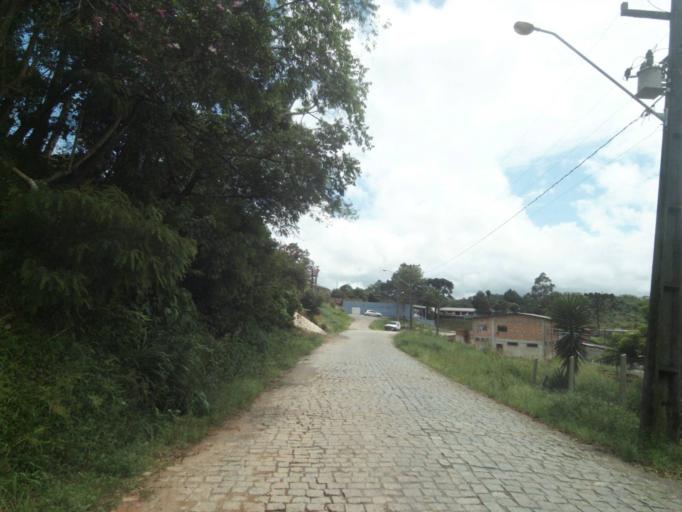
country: BR
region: Parana
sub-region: Campina Grande Do Sul
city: Campina Grande do Sul
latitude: -25.1091
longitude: -48.8078
